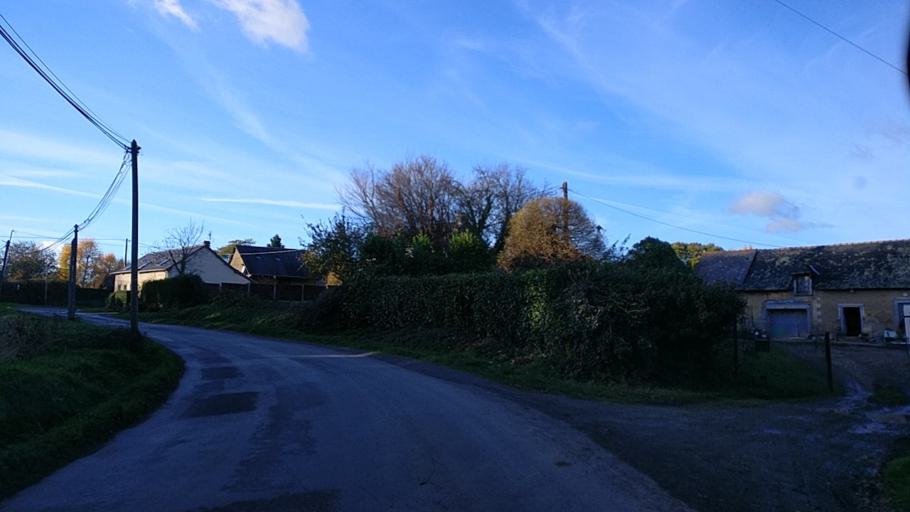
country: FR
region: Brittany
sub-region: Departement d'Ille-et-Vilaine
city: Acigne
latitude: 48.1500
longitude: -1.5479
